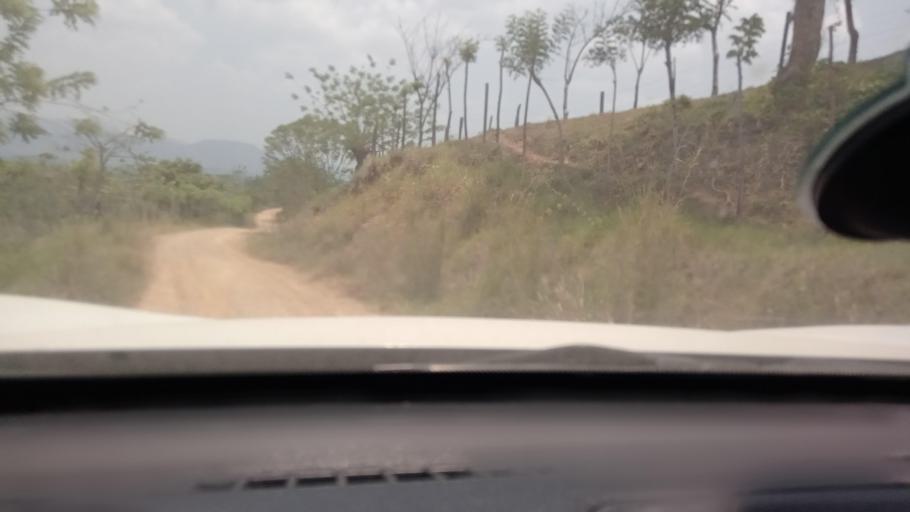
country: MX
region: Tabasco
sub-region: Huimanguillo
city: Francisco Rueda
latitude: 17.4933
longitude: -93.9232
